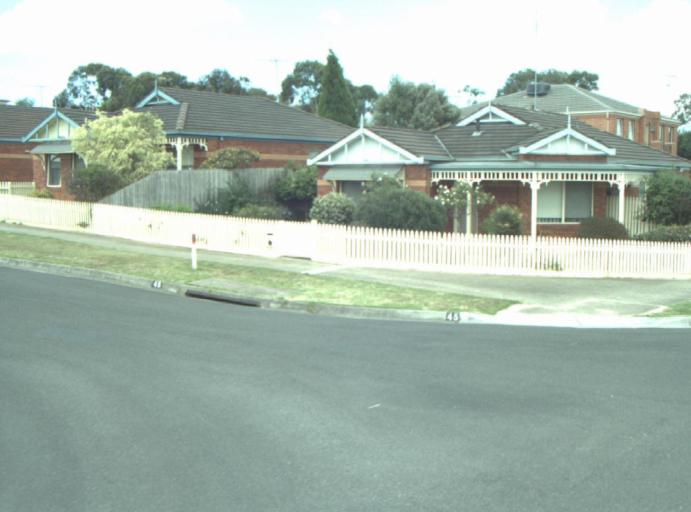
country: AU
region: Victoria
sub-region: Greater Geelong
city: Wandana Heights
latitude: -38.1933
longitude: 144.3192
